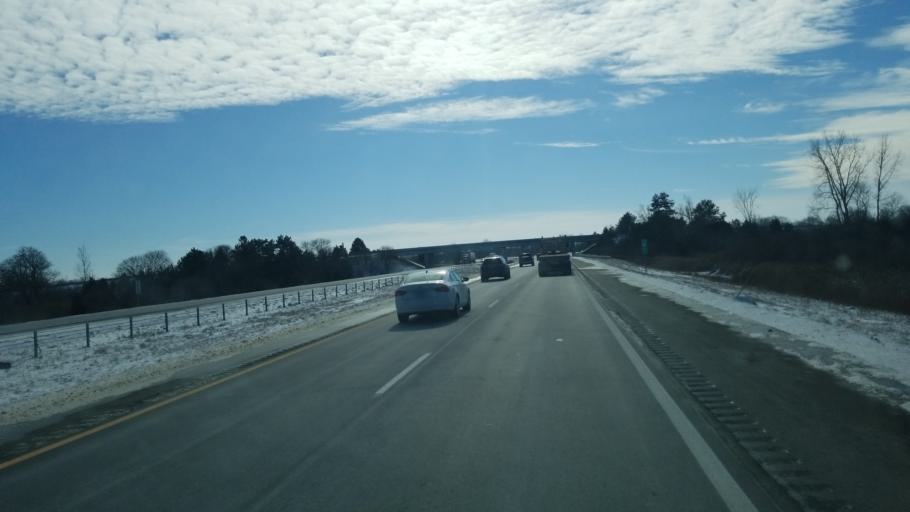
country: US
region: Michigan
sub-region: Washtenaw County
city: Milan
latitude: 42.0352
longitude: -83.6754
